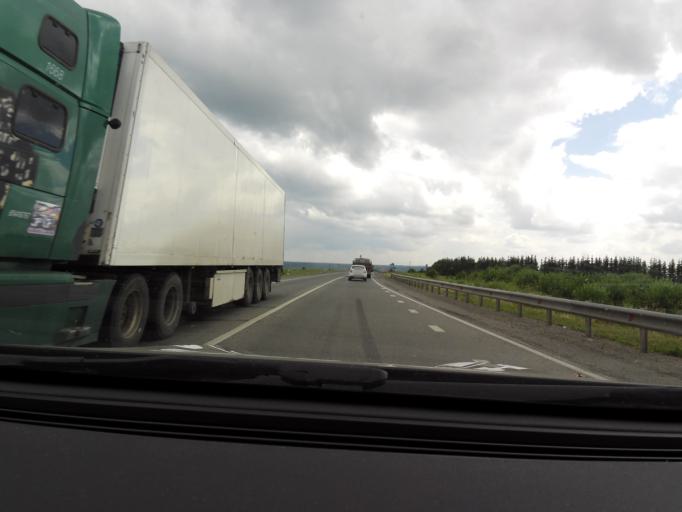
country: RU
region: Perm
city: Kungur
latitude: 57.4026
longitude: 56.8915
